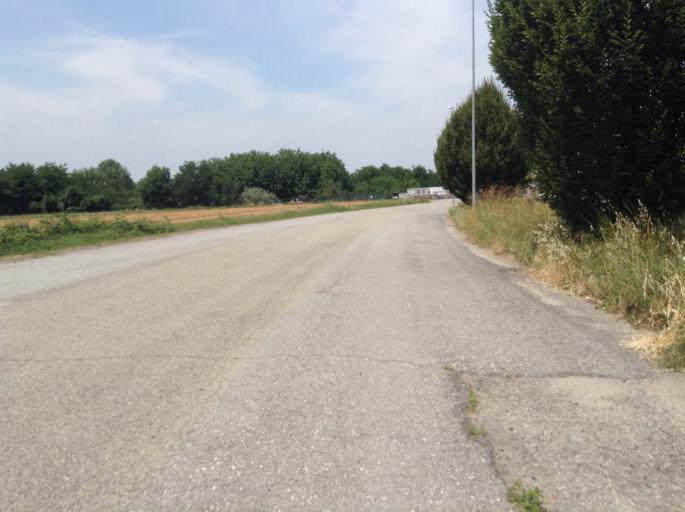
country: IT
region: Piedmont
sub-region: Provincia di Torino
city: Carignano
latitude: 44.8956
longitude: 7.6671
